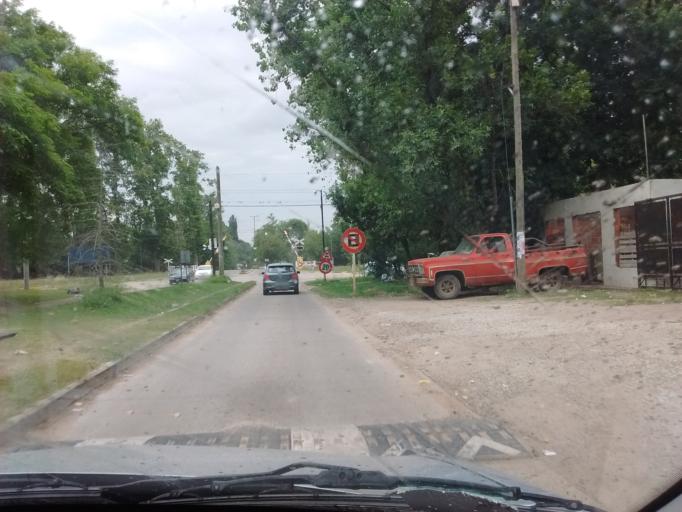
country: AR
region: Santa Fe
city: Funes
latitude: -32.9197
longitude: -60.7998
